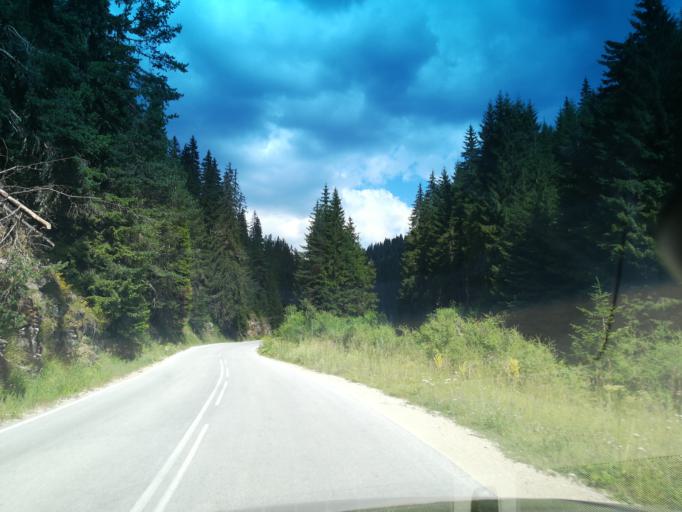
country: BG
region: Smolyan
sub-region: Obshtina Chepelare
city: Chepelare
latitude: 41.6618
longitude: 24.6497
